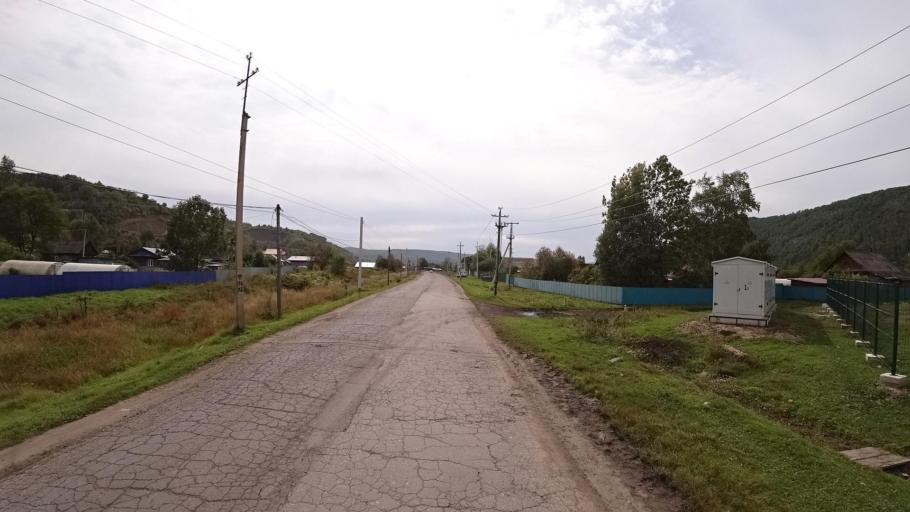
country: RU
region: Jewish Autonomous Oblast
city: Khingansk
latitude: 49.0026
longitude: 131.0543
